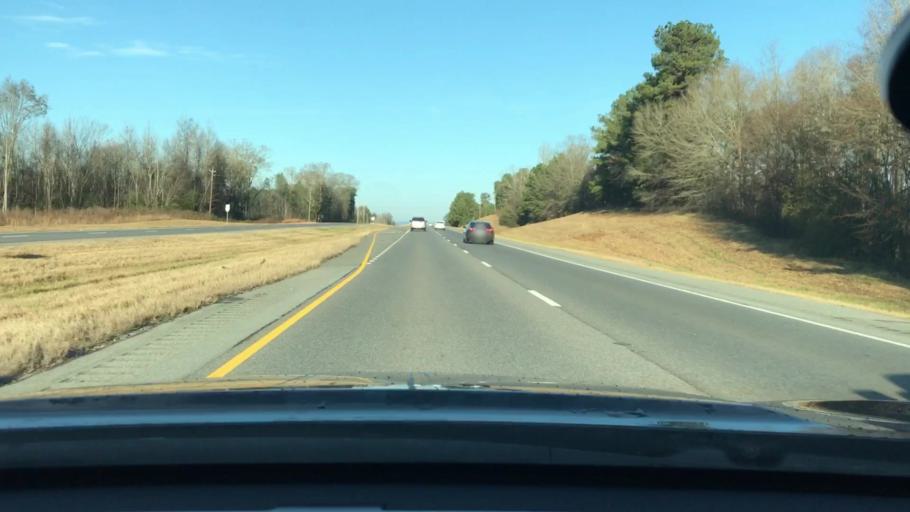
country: US
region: Alabama
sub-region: Talladega County
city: Childersburg
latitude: 33.3109
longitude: -86.3846
